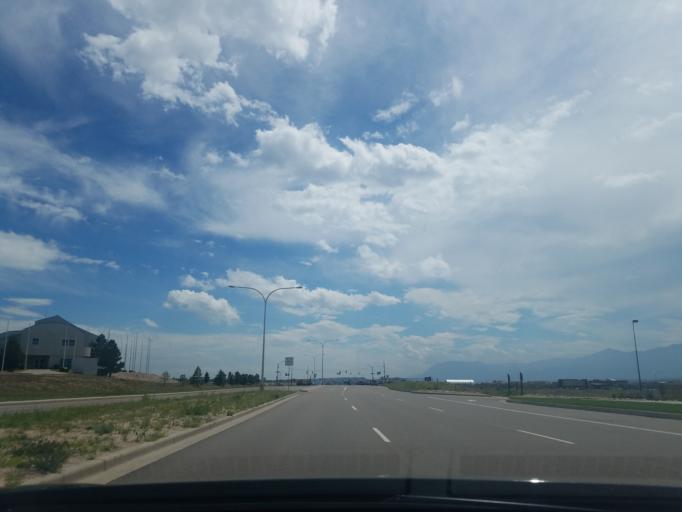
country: US
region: Colorado
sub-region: El Paso County
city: Gleneagle
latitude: 38.9932
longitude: -104.7981
